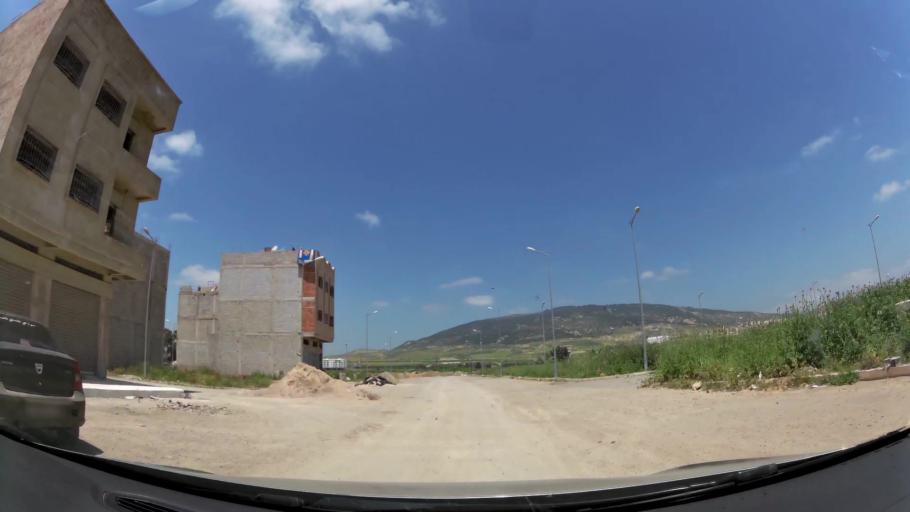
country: MA
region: Fes-Boulemane
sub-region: Fes
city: Fes
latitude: 34.0375
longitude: -5.0568
